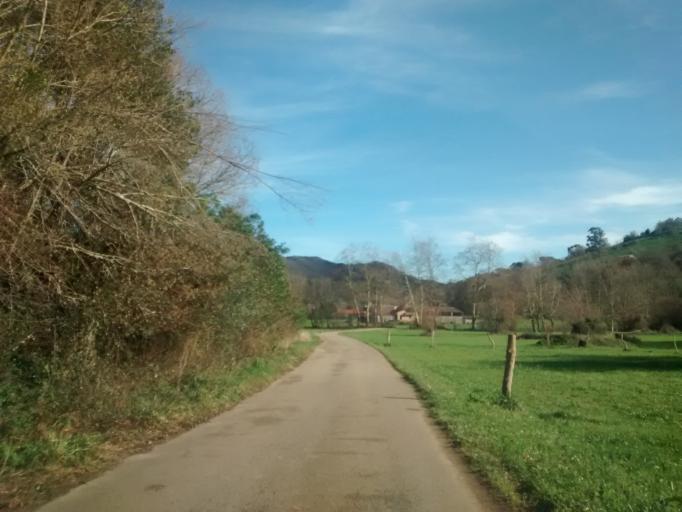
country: ES
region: Cantabria
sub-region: Provincia de Cantabria
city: Entrambasaguas
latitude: 43.3403
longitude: -3.6889
